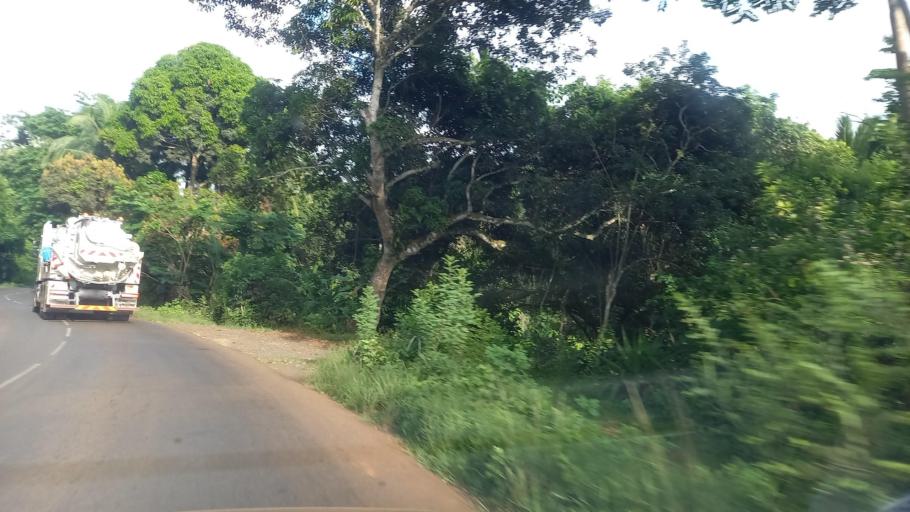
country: YT
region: Chiconi
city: Chiconi
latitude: -12.8170
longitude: 45.1310
